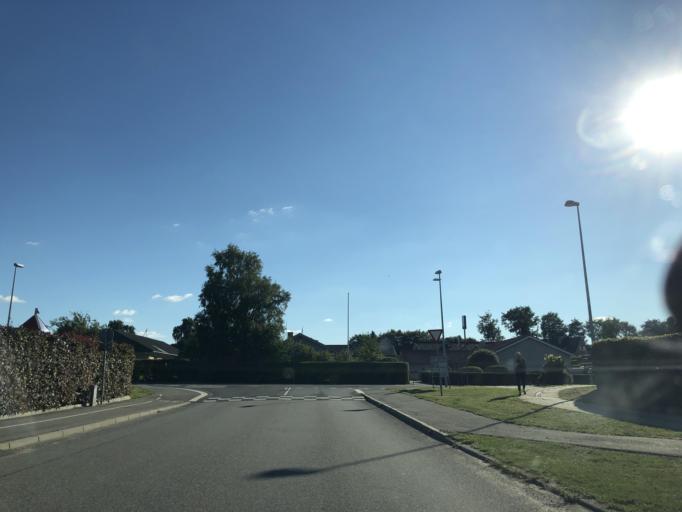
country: DK
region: North Denmark
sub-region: Mariagerfjord Kommune
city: Hobro
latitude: 56.6329
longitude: 9.8124
